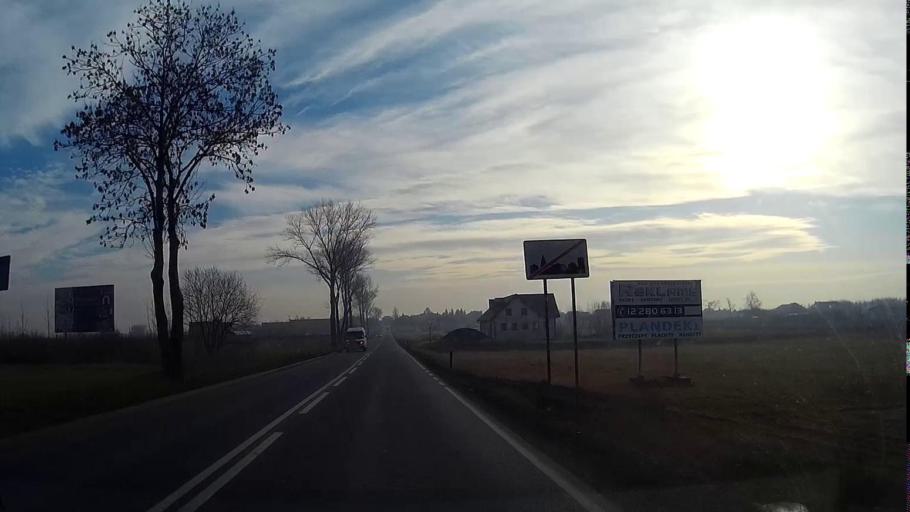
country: PL
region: Lesser Poland Voivodeship
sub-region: Powiat krakowski
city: Liszki
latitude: 50.0364
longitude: 19.7477
